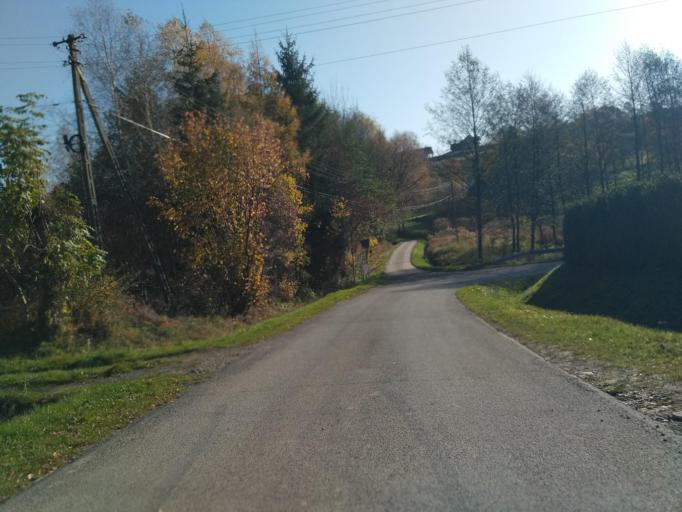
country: PL
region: Subcarpathian Voivodeship
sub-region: Powiat rzeszowski
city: Blazowa
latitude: 49.8724
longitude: 22.1181
